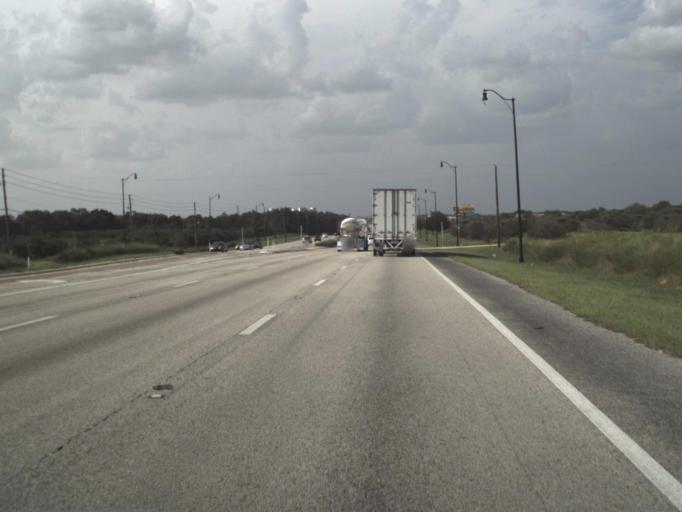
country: US
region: Florida
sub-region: Polk County
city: Davenport
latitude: 28.1675
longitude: -81.6397
